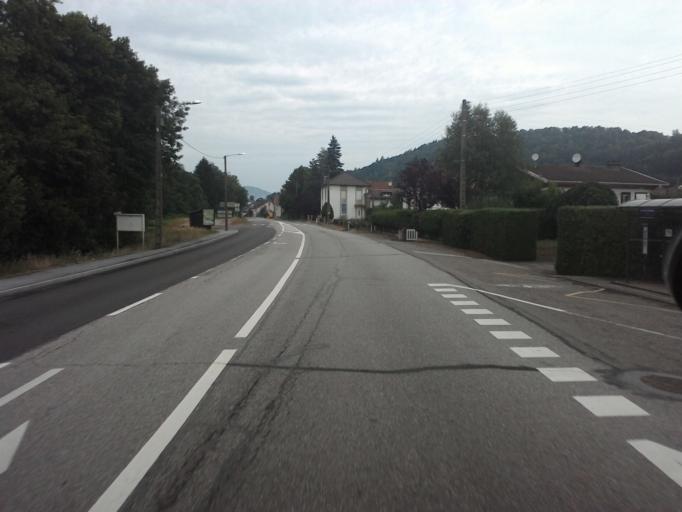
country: FR
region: Lorraine
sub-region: Departement des Vosges
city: Fresse-sur-Moselle
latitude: 47.8754
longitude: 6.7838
